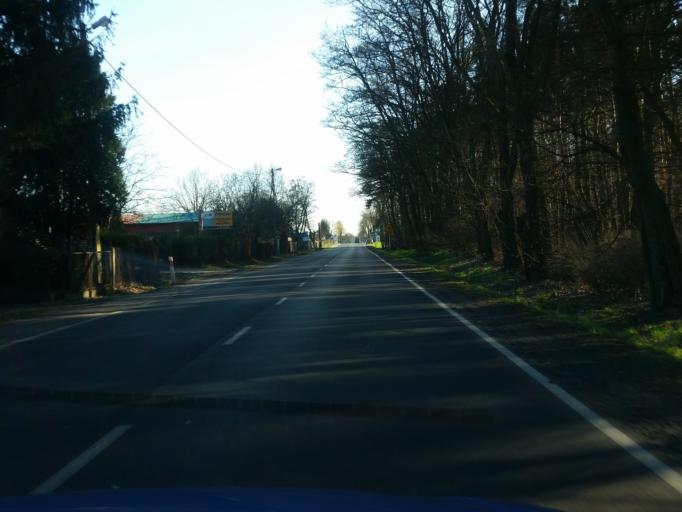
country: PL
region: Lodz Voivodeship
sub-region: Powiat radomszczanski
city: Gomunice
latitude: 51.1639
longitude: 19.4922
